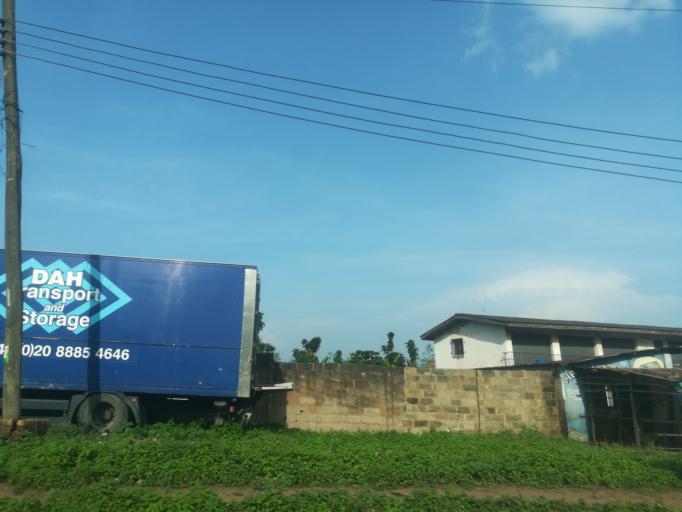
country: NG
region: Oyo
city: Moniya
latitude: 7.4963
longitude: 3.9141
